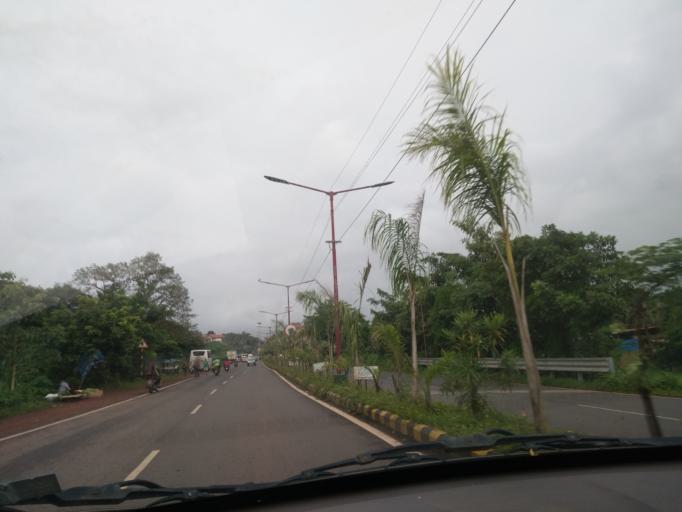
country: IN
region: Goa
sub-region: South Goa
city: Raia
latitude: 15.2885
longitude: 73.9775
